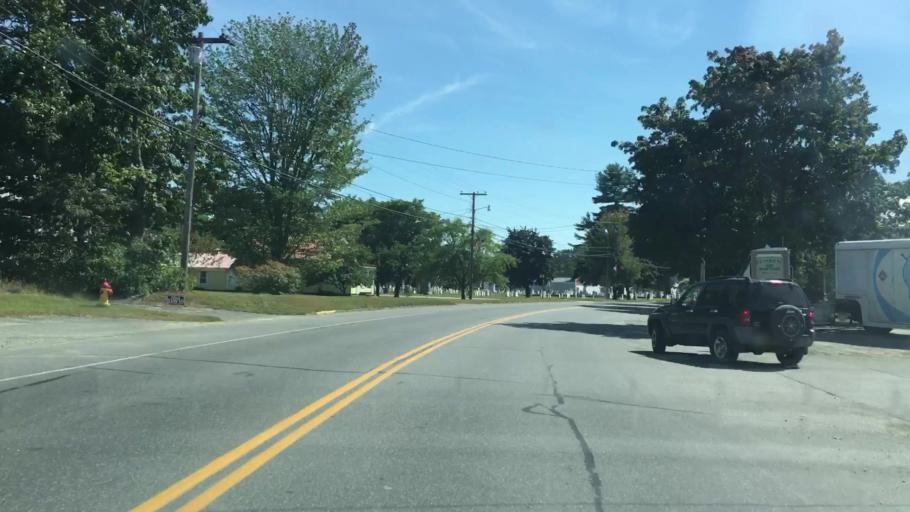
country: US
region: Maine
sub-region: Piscataquis County
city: Milo
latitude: 45.2611
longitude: -68.9885
